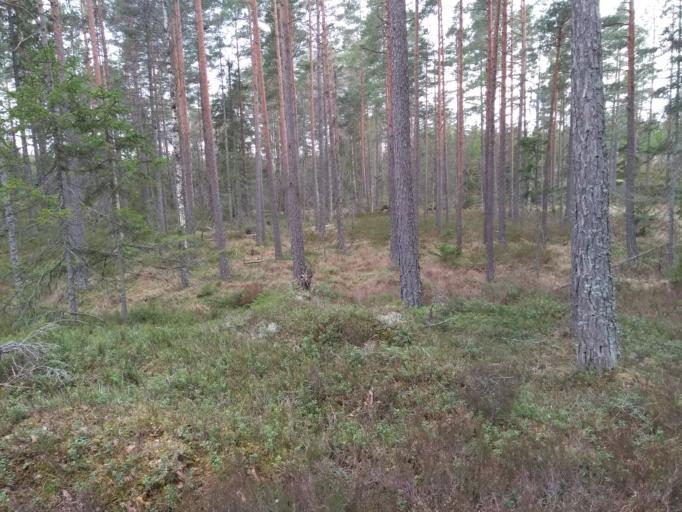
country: SE
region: OEstergoetland
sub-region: Norrkopings Kommun
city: Krokek
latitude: 58.7182
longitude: 16.4618
